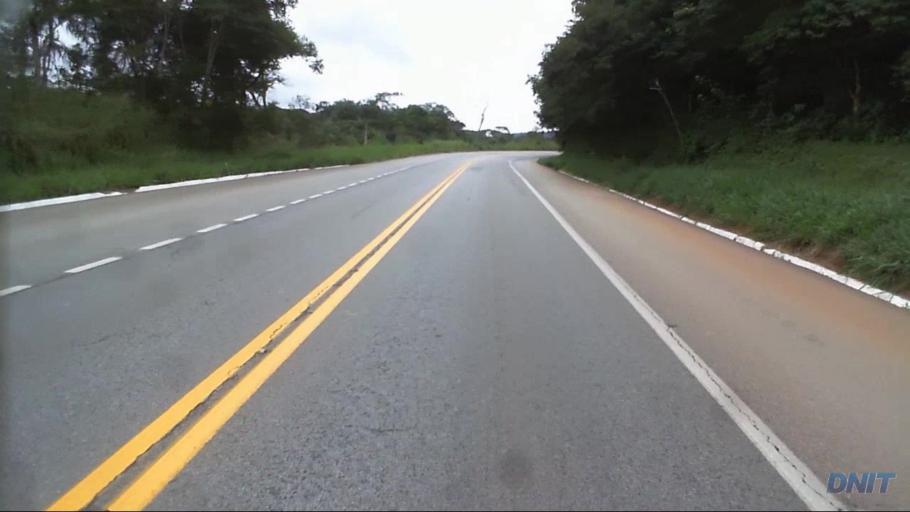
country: BR
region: Minas Gerais
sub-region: Barao De Cocais
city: Barao de Cocais
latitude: -19.7486
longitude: -43.4901
